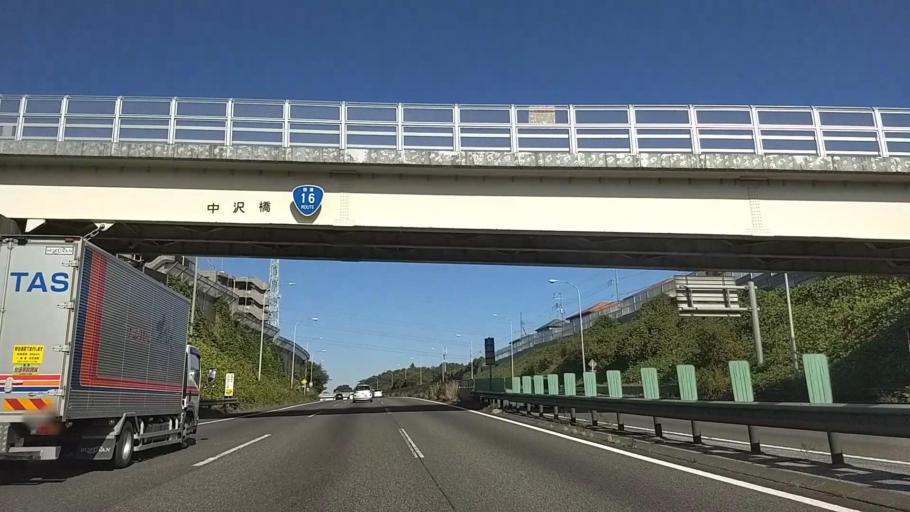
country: JP
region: Kanagawa
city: Minami-rinkan
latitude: 35.4699
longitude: 139.5330
